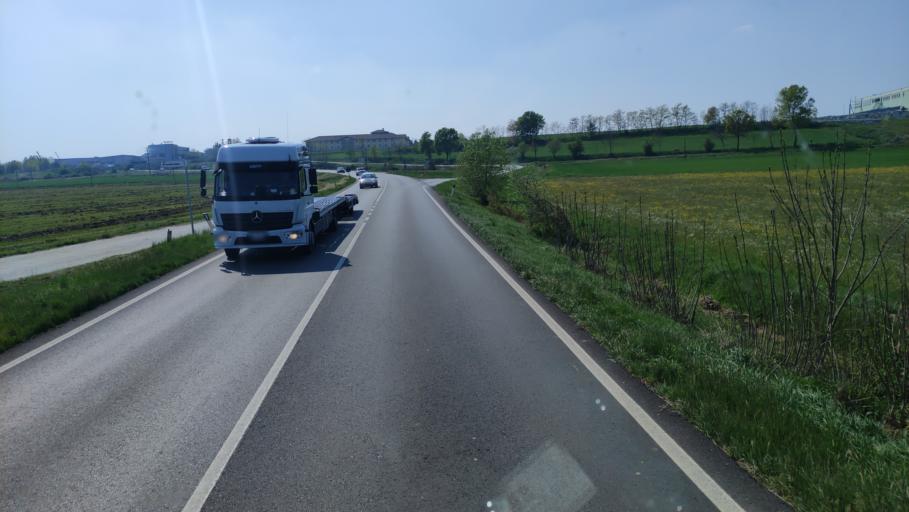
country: IT
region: Piedmont
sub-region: Provincia di Cuneo
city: Marene
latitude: 44.6661
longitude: 7.7550
